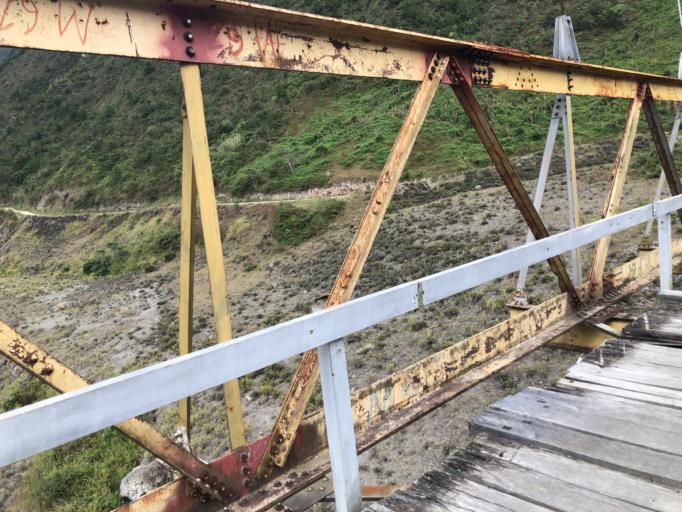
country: CO
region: Cauca
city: Belalcazar
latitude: 2.7454
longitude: -76.0395
